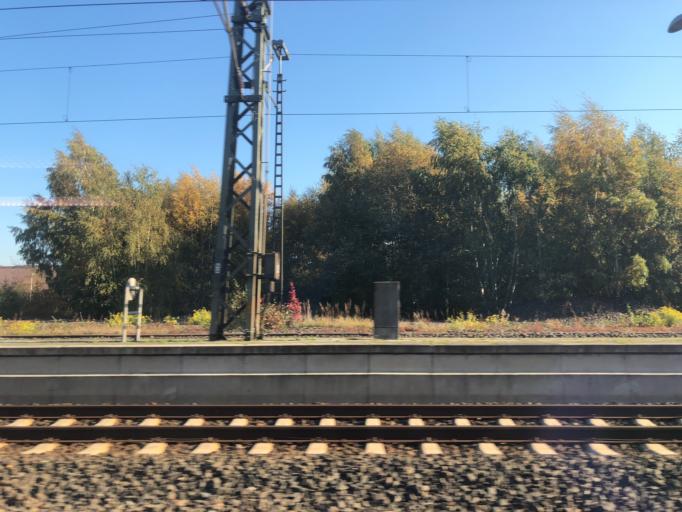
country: DE
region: Schleswig-Holstein
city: Rendsburg
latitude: 54.3007
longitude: 9.6730
